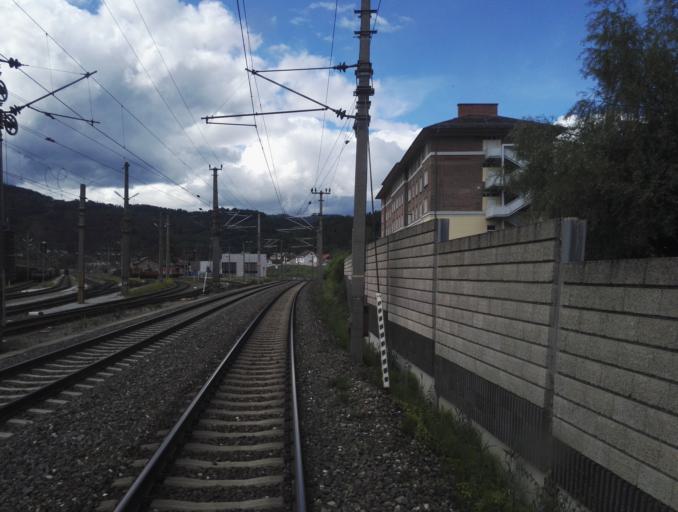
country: AT
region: Styria
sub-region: Politischer Bezirk Bruck-Muerzzuschlag
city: Bruck an der Mur
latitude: 47.4221
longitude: 15.2799
